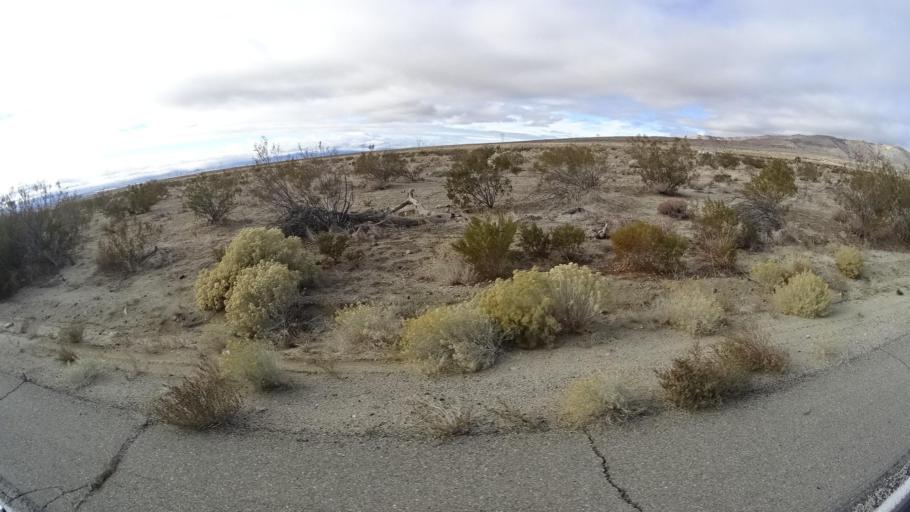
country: US
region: California
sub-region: Kern County
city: Mojave
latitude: 34.9828
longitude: -118.3162
